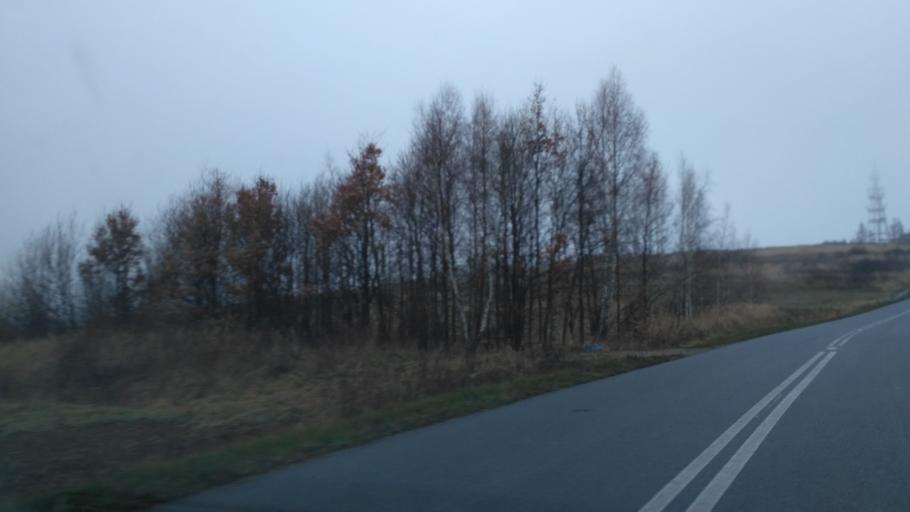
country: PL
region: Subcarpathian Voivodeship
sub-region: Powiat jaroslawski
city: Jodlowka
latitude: 49.8975
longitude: 22.4835
